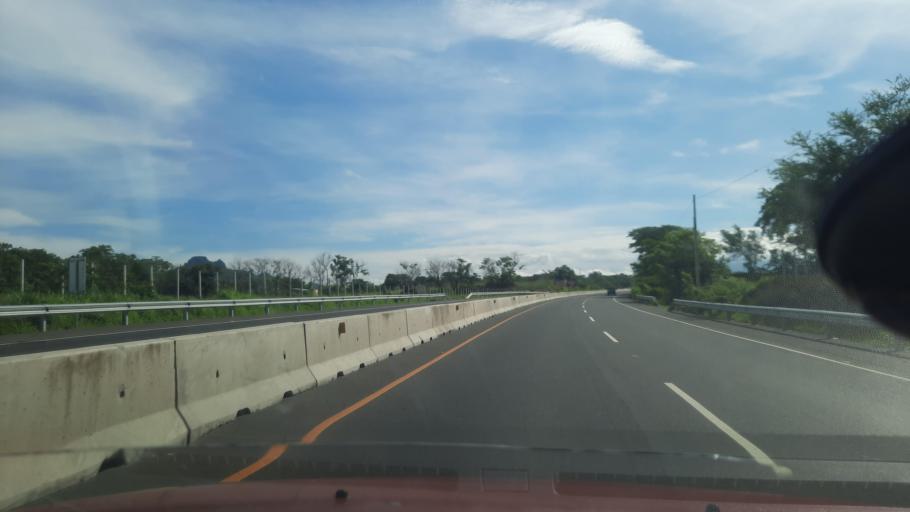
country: SV
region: La Paz
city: El Rosario
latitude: 13.4737
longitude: -89.0028
